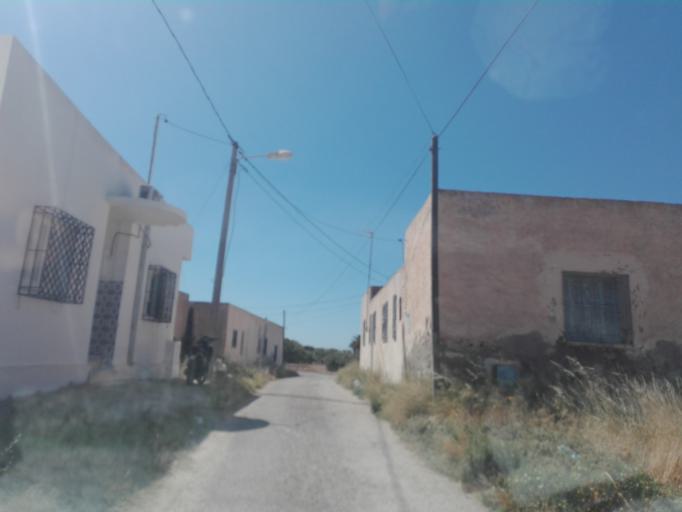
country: TN
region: Safaqis
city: Jabinyanah
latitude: 34.7196
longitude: 11.2420
